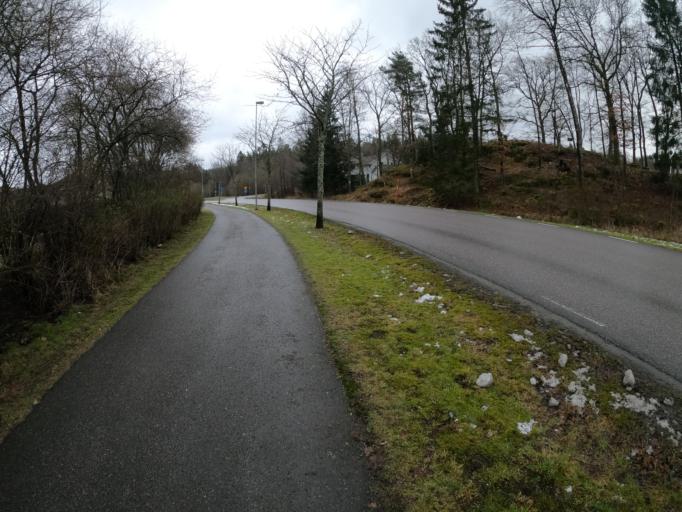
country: SE
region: Vaestra Goetaland
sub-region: Harryda Kommun
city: Molnlycke
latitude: 57.6432
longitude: 12.1068
